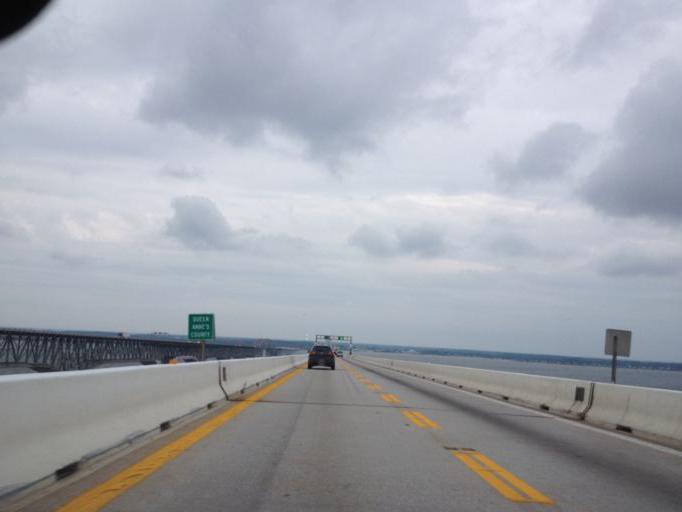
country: US
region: Maryland
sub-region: Queen Anne's County
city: Stevensville
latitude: 38.9914
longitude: -76.3745
